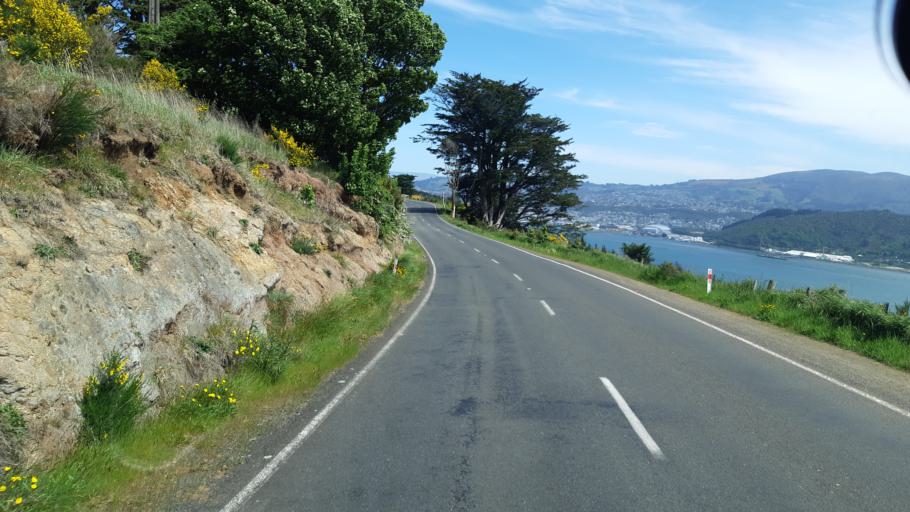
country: NZ
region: Otago
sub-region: Dunedin City
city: Dunedin
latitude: -45.8850
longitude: 170.5790
